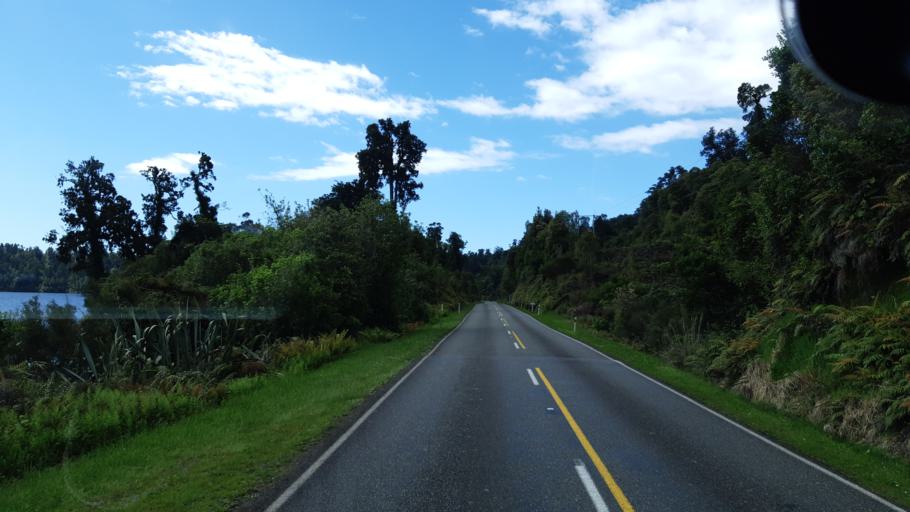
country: NZ
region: West Coast
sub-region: Westland District
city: Hokitika
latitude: -43.0561
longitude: 170.6363
